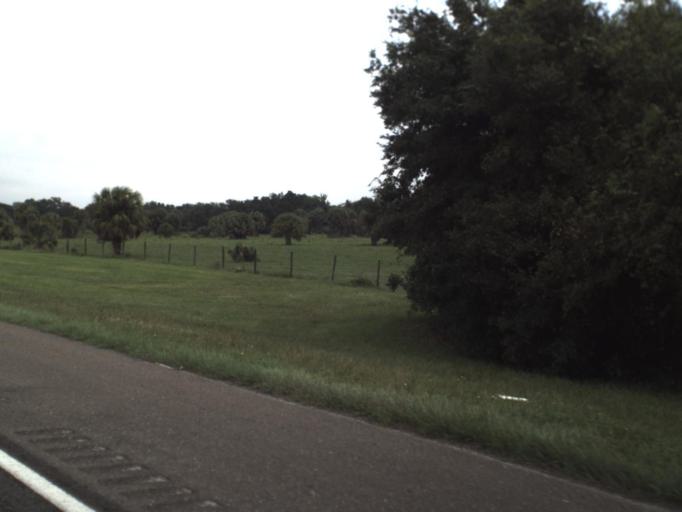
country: US
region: Florida
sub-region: Hillsborough County
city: Ruskin
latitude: 27.6357
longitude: -82.4661
